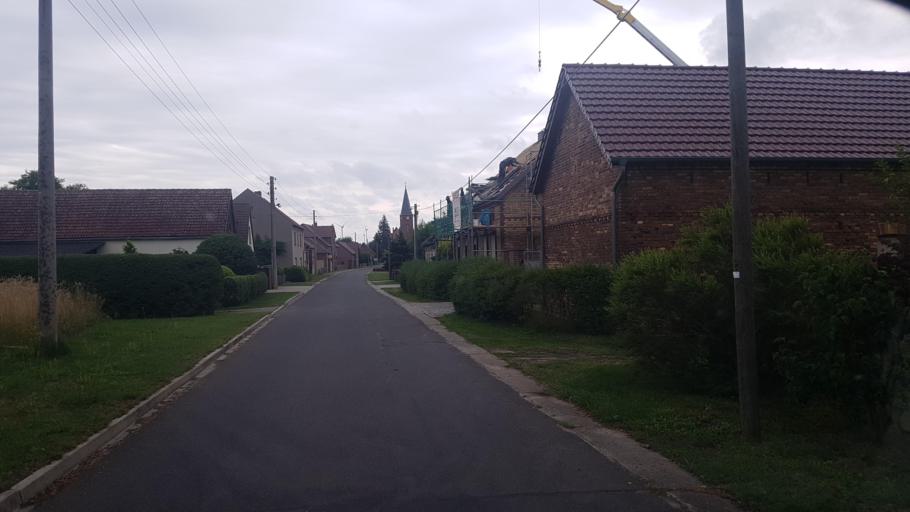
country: DE
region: Brandenburg
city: Crinitz
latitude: 51.7344
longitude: 13.8237
